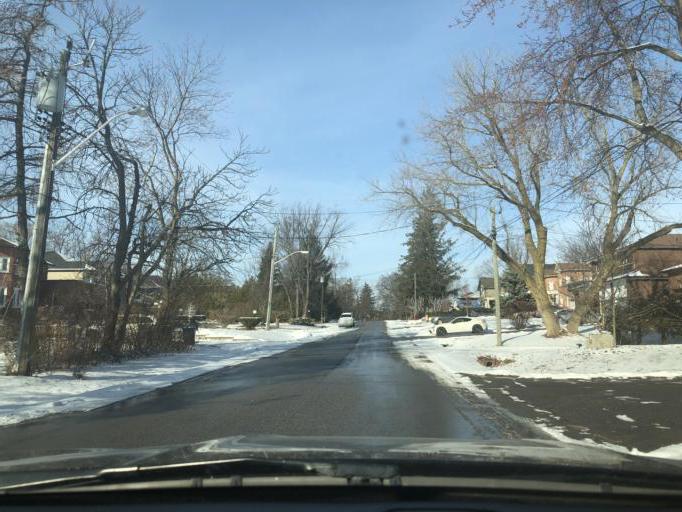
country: CA
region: Ontario
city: Scarborough
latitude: 43.7883
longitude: -79.1547
